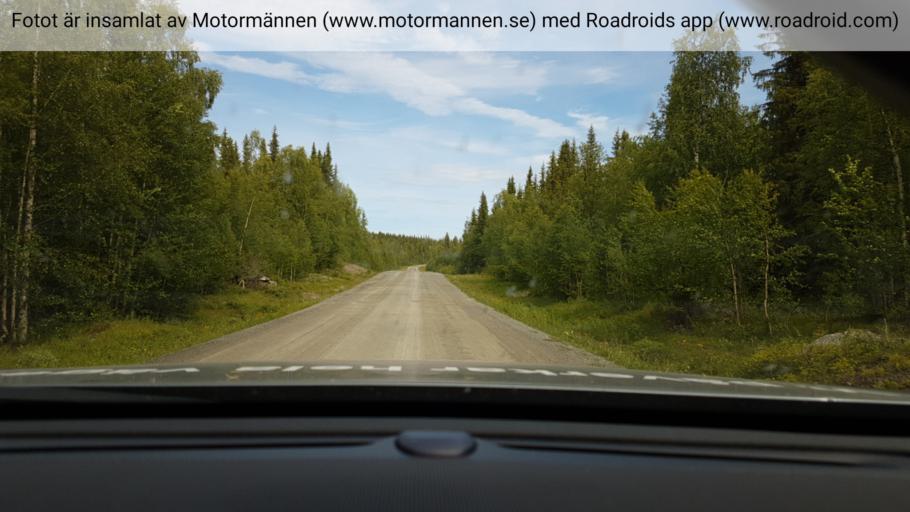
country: SE
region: Vaesterbotten
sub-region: Storumans Kommun
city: Fristad
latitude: 65.1789
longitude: 16.3783
